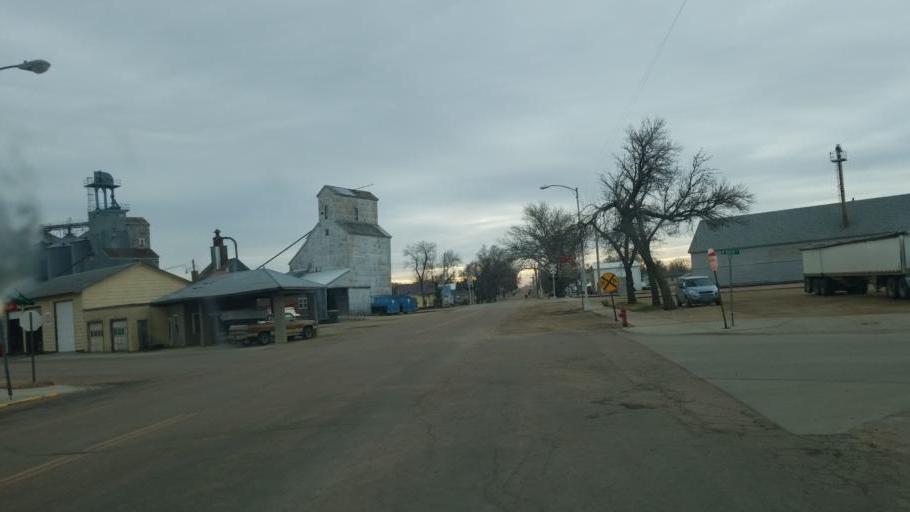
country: US
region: South Dakota
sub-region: Hutchinson County
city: Parkston
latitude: 43.2238
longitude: -97.9656
